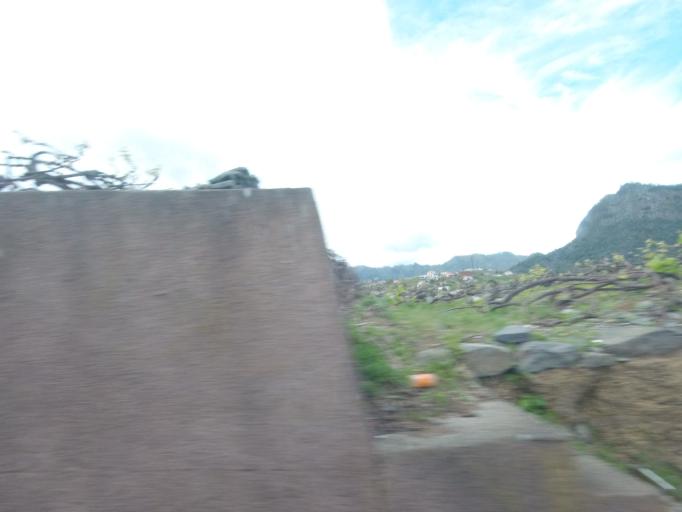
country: PT
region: Madeira
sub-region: Santana
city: Santana
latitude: 32.7638
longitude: -16.8275
